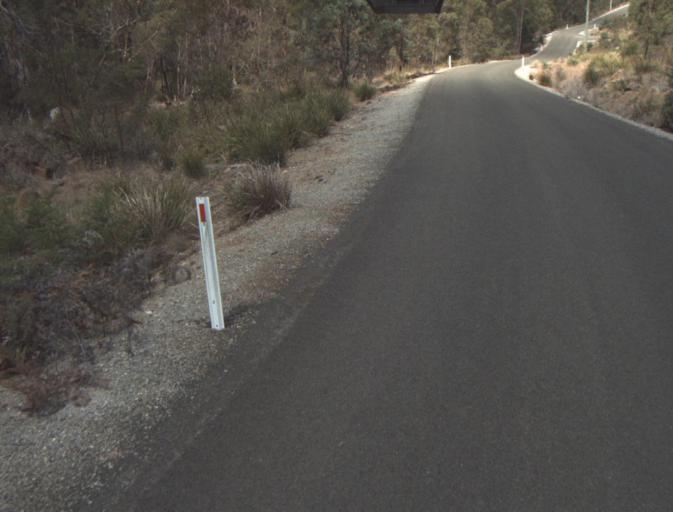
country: AU
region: Tasmania
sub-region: Launceston
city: Mayfield
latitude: -41.3219
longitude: 147.1231
